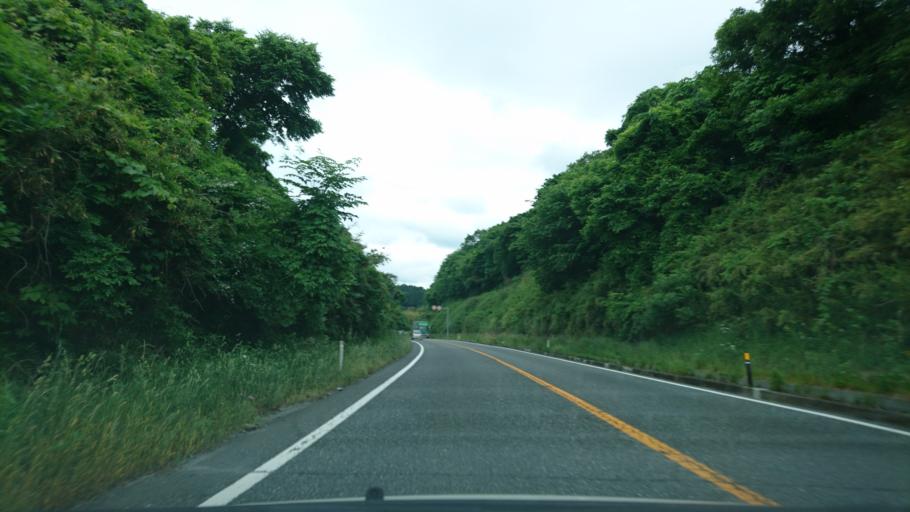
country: JP
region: Iwate
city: Ichinoseki
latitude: 38.8969
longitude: 141.1149
